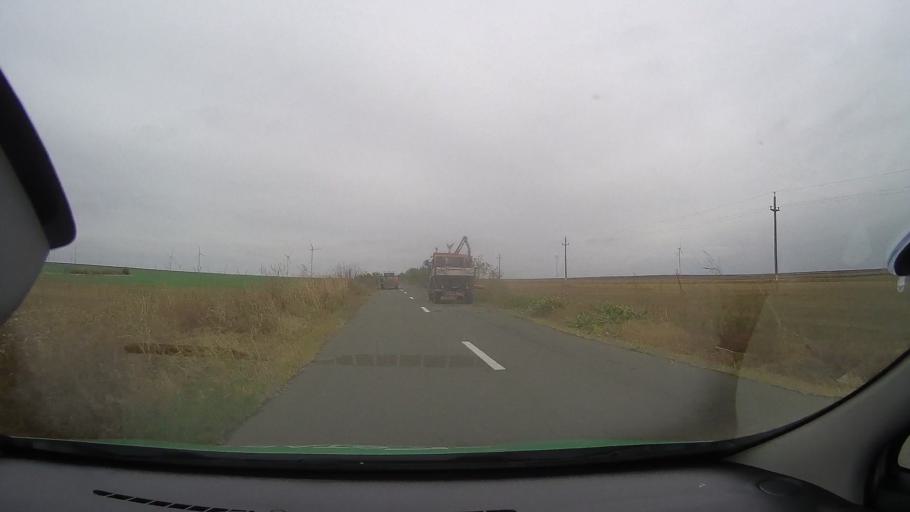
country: RO
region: Constanta
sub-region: Comuna Targusor
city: Targusor
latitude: 44.4701
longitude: 28.3885
